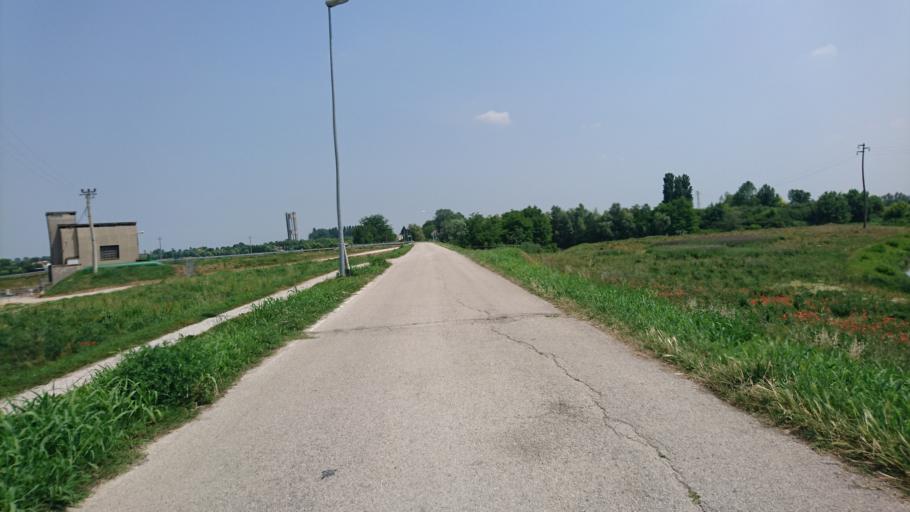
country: IT
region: Veneto
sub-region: Provincia di Padova
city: Cartura
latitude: 45.2888
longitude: 11.8587
